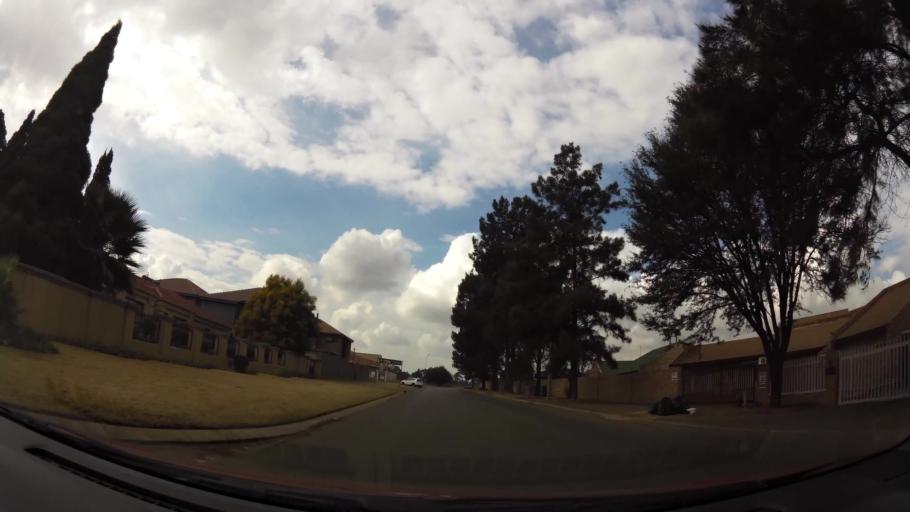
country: ZA
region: Gauteng
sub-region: Sedibeng District Municipality
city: Vanderbijlpark
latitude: -26.7381
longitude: 27.8537
